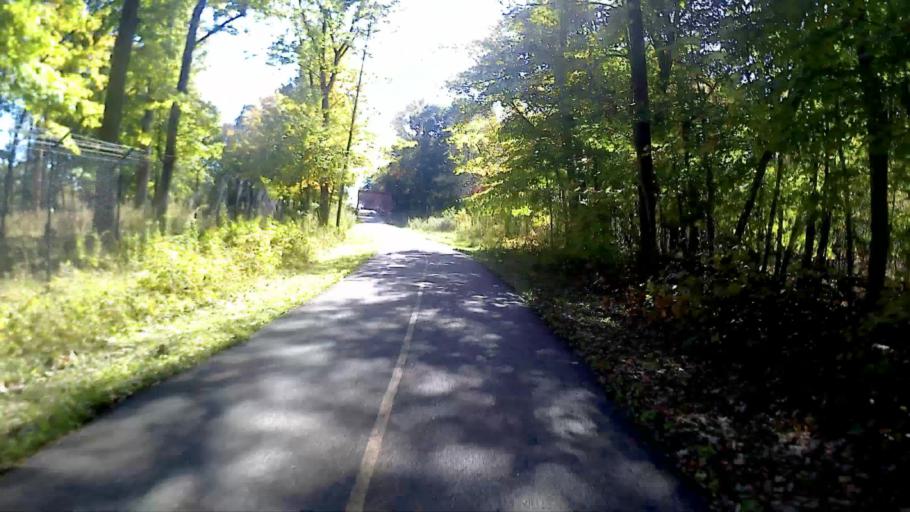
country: US
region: Illinois
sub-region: Cook County
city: Elk Grove Village
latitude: 42.0303
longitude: -87.9905
